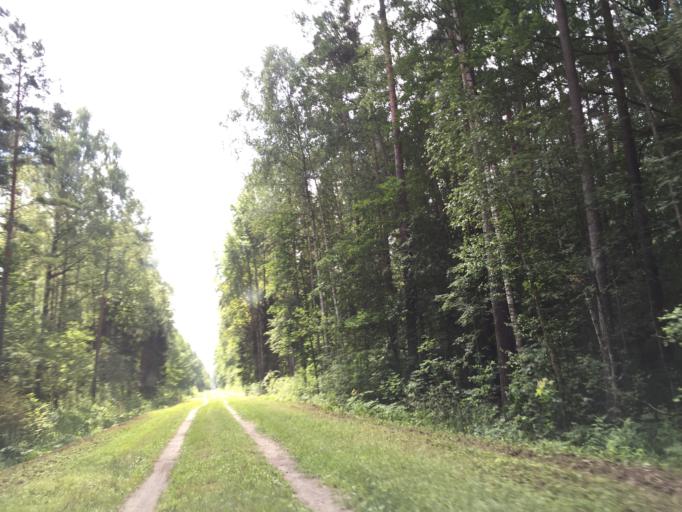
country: LV
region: Ozolnieku
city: Ozolnieki
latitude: 56.6839
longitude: 23.7526
